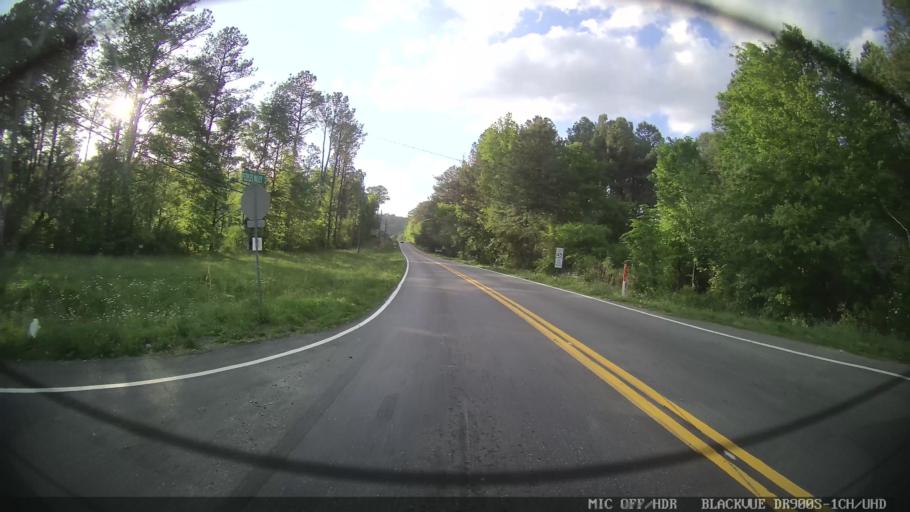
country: US
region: Georgia
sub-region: Bartow County
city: Cartersville
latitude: 34.2378
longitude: -84.8060
